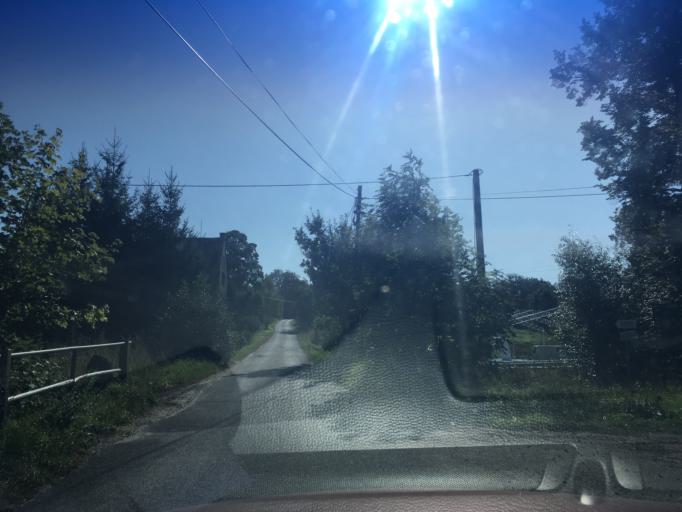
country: PL
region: Lower Silesian Voivodeship
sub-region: Powiat lubanski
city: Lesna
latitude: 51.0062
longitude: 15.1943
